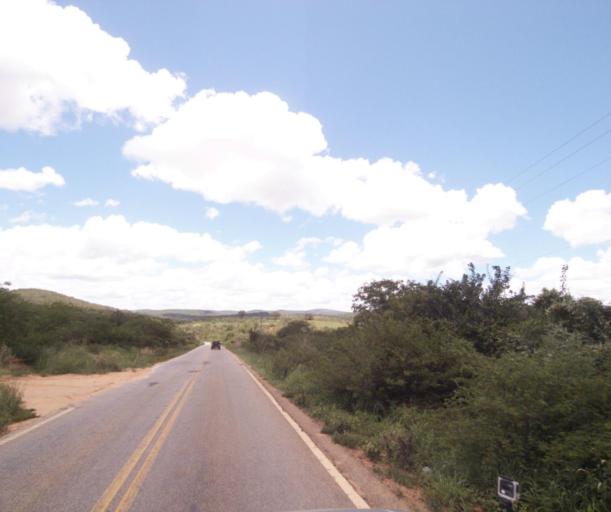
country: BR
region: Bahia
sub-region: Pocoes
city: Pocoes
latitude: -14.3809
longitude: -40.5112
